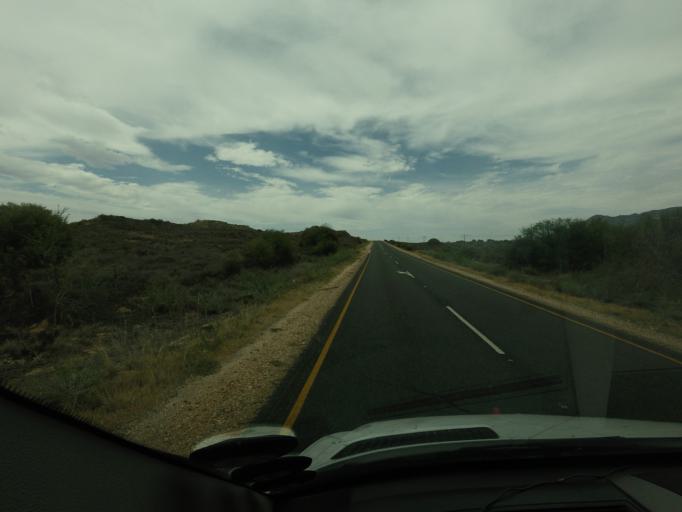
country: ZA
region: Western Cape
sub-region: Overberg District Municipality
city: Swellendam
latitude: -33.8521
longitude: 20.8220
